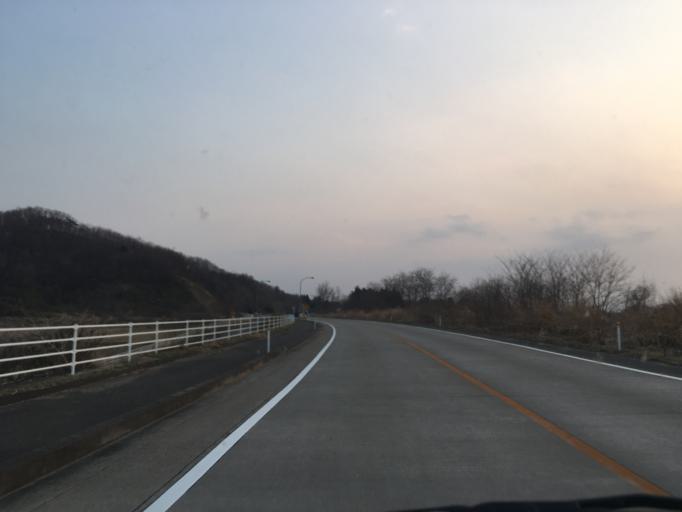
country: JP
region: Fukushima
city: Koriyama
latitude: 37.4339
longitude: 140.4264
